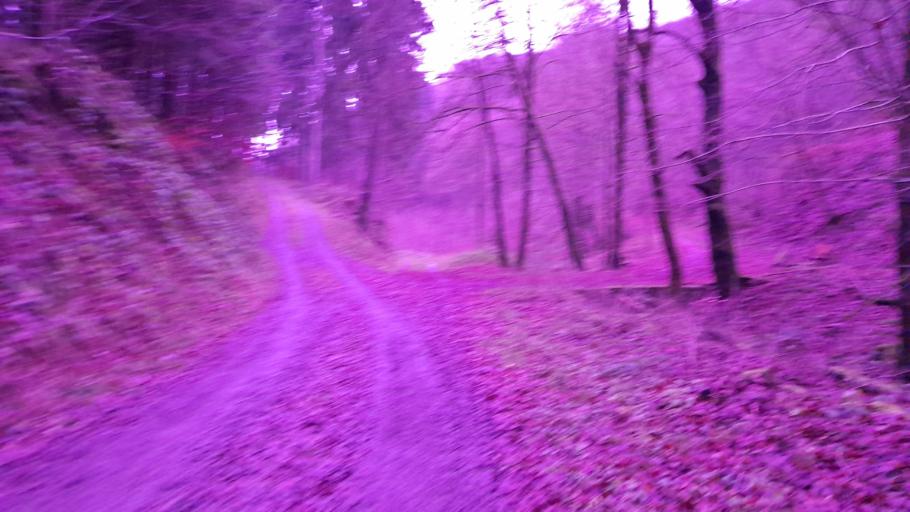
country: DE
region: Rheinland-Pfalz
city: Dasburg
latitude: 50.0762
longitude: 6.1038
